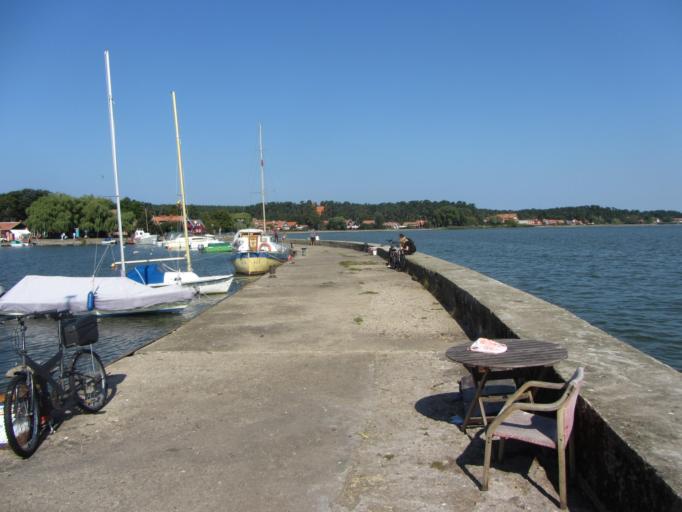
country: LT
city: Nida
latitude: 55.3033
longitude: 21.0098
